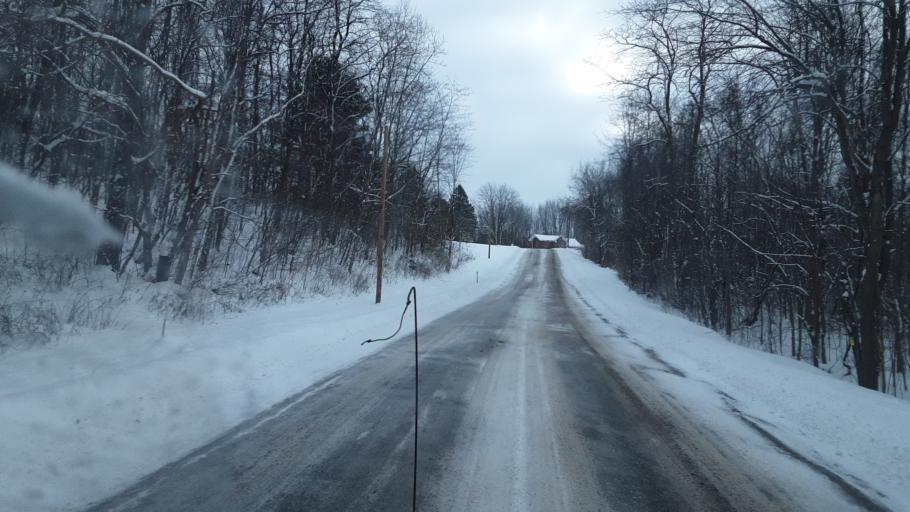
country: US
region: New York
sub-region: Wayne County
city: Lyons
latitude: 43.1389
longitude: -76.9963
